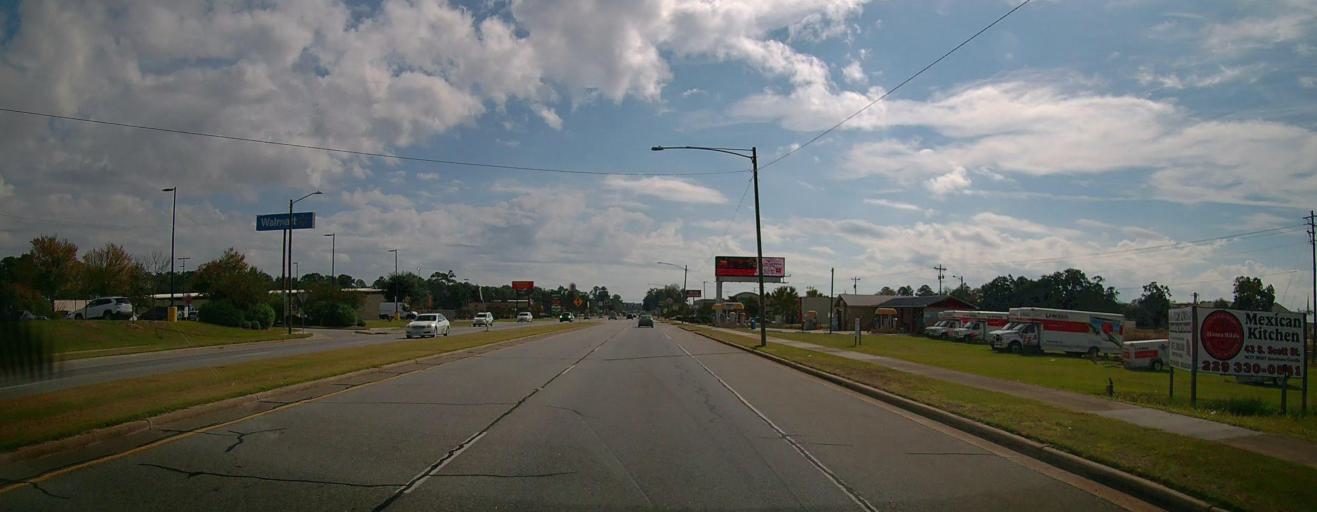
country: US
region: Georgia
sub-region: Mitchell County
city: Camilla
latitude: 31.2362
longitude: -84.2001
